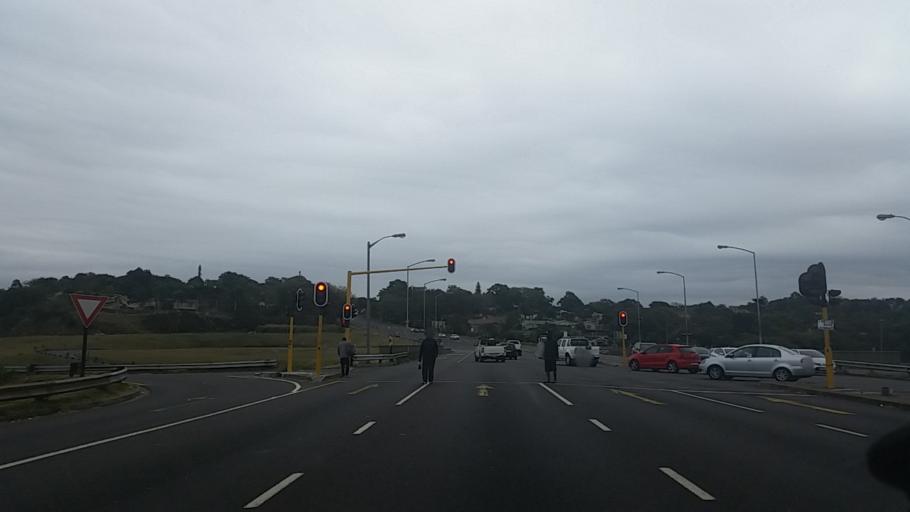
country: ZA
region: KwaZulu-Natal
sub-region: eThekwini Metropolitan Municipality
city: Berea
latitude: -29.8489
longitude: 30.9315
